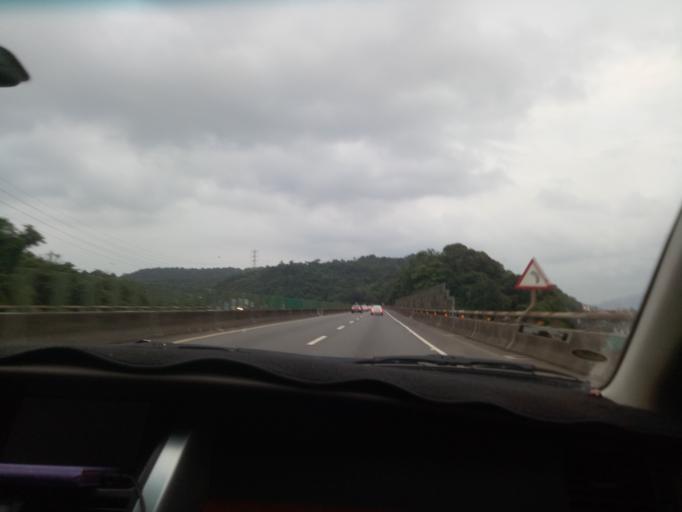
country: TW
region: Taiwan
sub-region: Keelung
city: Keelung
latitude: 25.1037
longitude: 121.7576
